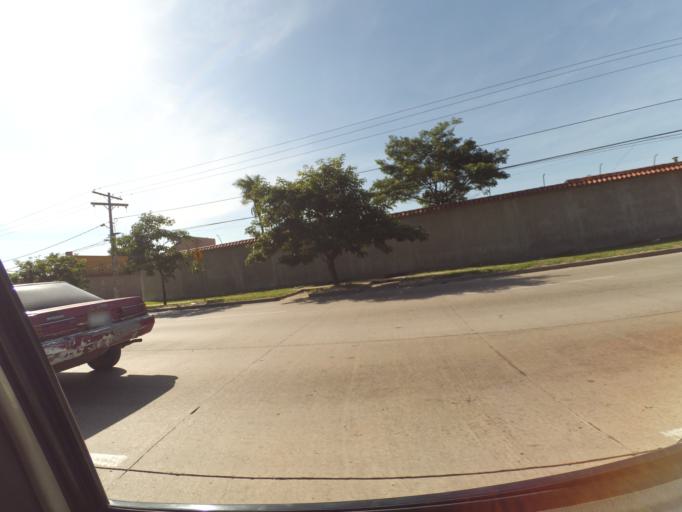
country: BO
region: Santa Cruz
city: Santa Cruz de la Sierra
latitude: -17.8143
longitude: -63.1648
